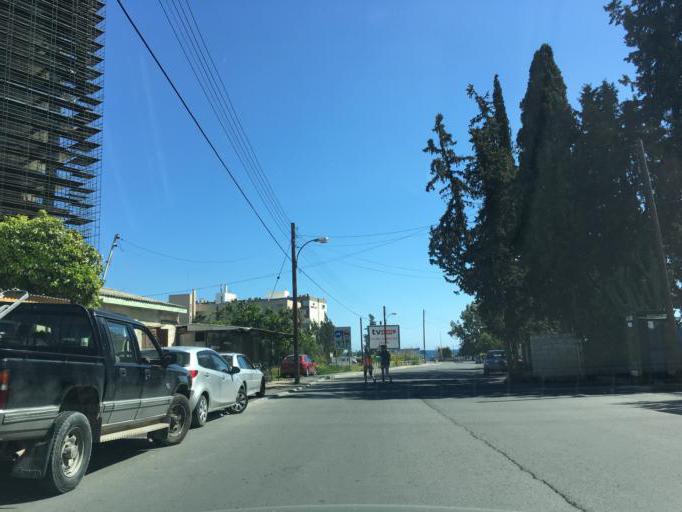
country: CY
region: Limassol
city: Limassol
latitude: 34.6903
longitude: 33.0693
